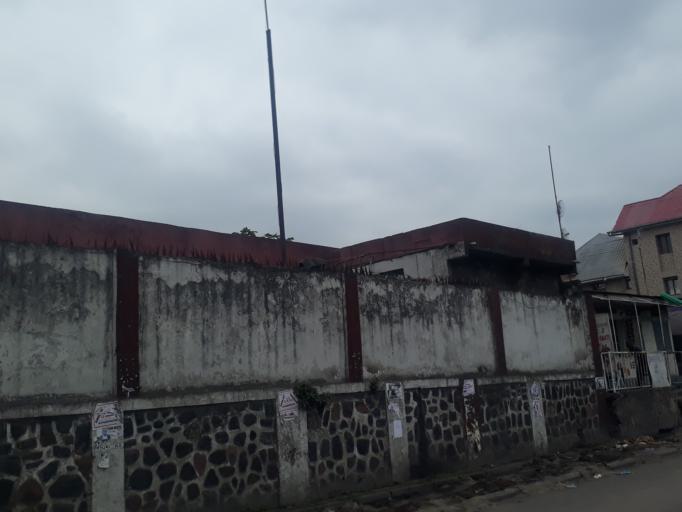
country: CD
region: Kinshasa
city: Kinshasa
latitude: -4.3186
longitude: 15.3109
